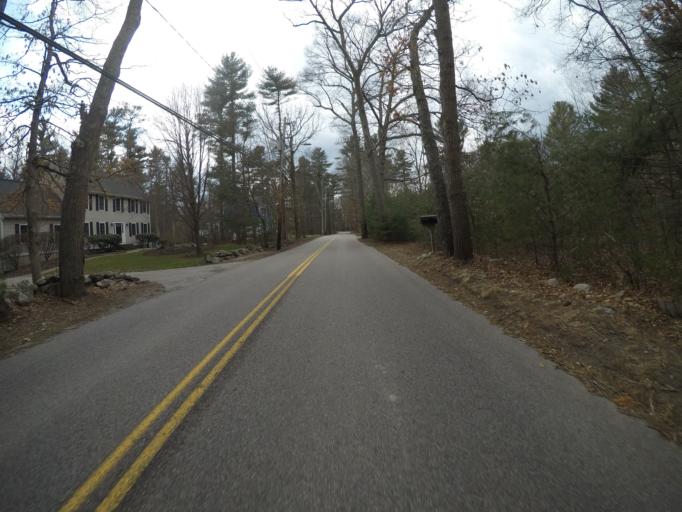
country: US
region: Massachusetts
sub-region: Bristol County
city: Easton
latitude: 42.0472
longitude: -71.1197
